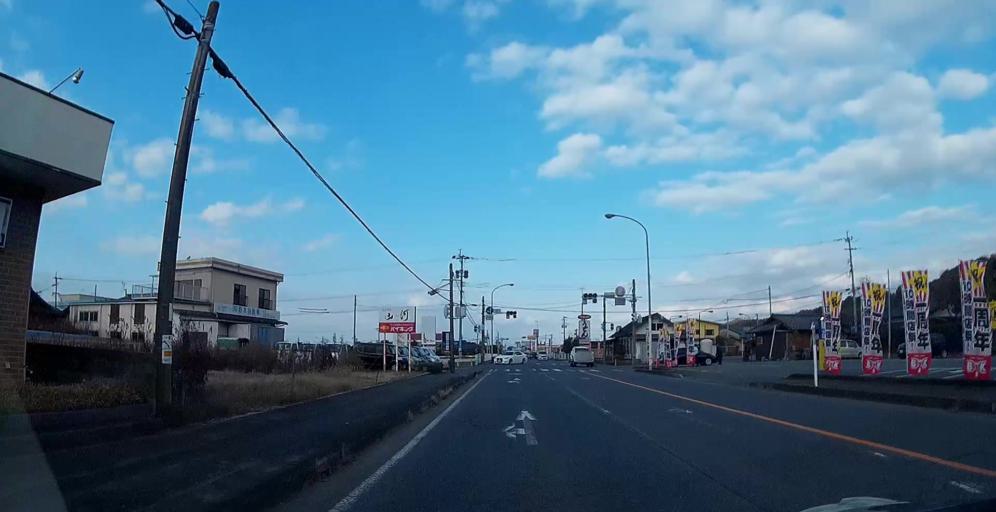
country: JP
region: Kumamoto
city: Yatsushiro
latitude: 32.5498
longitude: 130.6785
